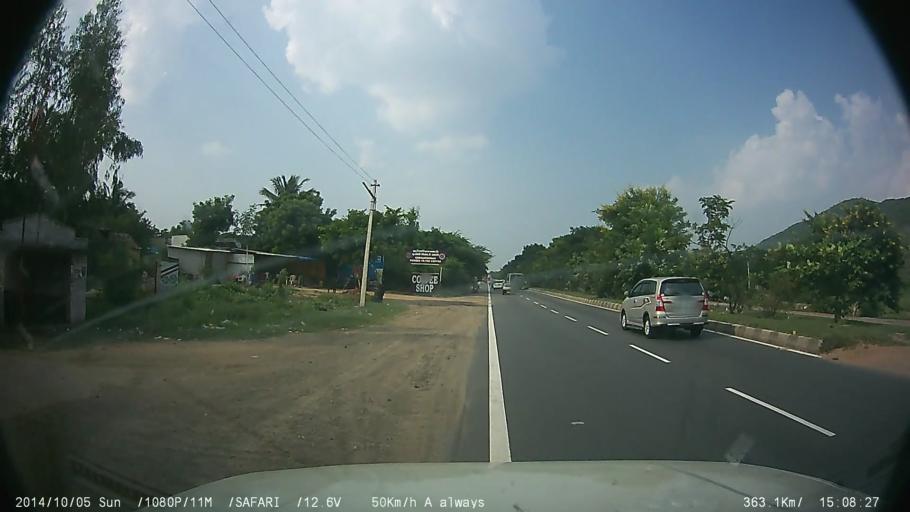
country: IN
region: Tamil Nadu
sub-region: Kancheepuram
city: Chengalpattu
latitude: 12.6700
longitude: 79.9586
